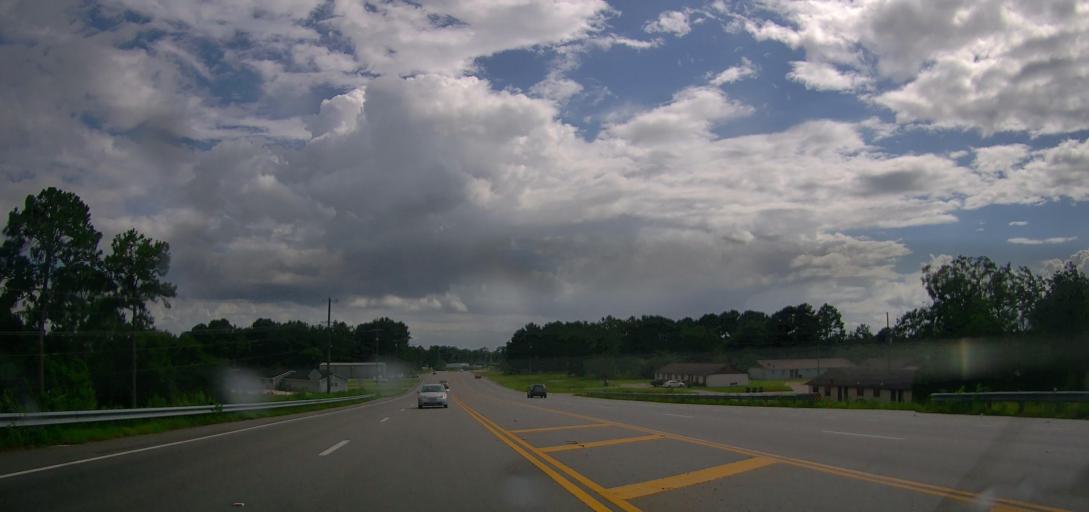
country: US
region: Georgia
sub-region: Coffee County
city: Douglas
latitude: 31.5016
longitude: -82.8275
